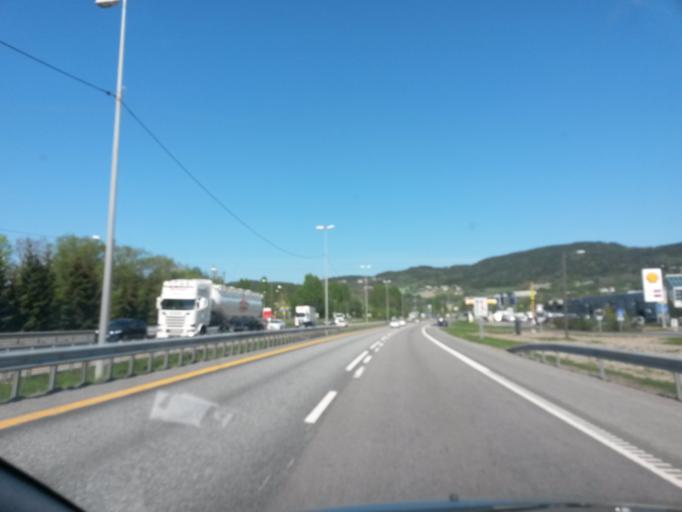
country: NO
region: Buskerud
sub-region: Lier
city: Lierbyen
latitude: 59.7663
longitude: 10.2562
